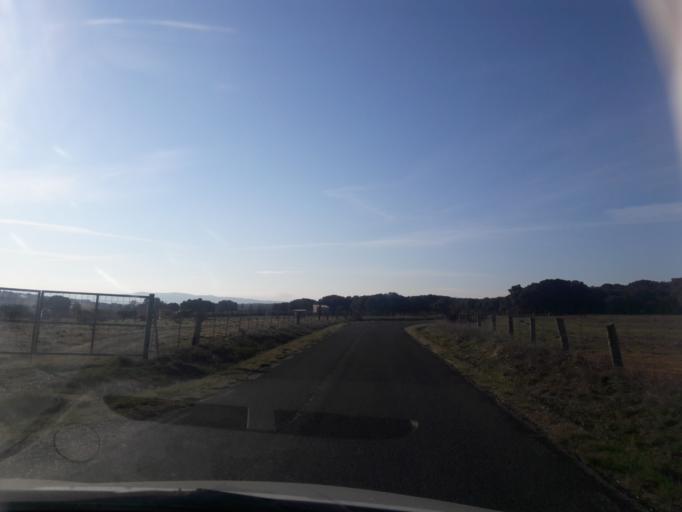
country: ES
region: Castille and Leon
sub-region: Provincia de Salamanca
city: Montejo
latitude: 40.6234
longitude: -5.6105
